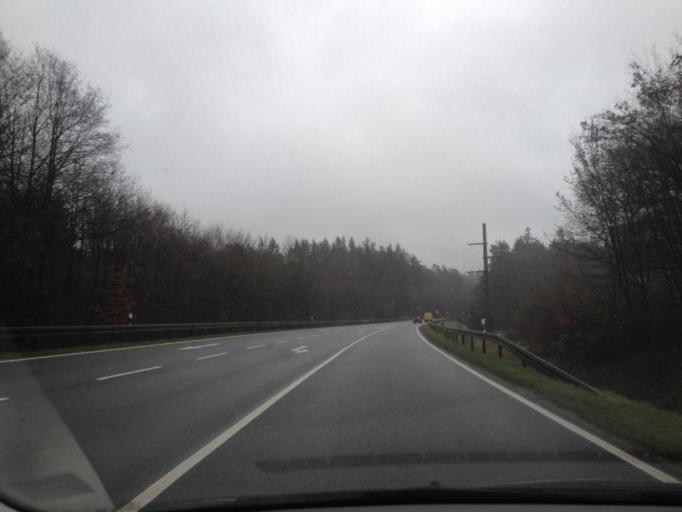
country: DE
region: Bavaria
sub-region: Regierungsbezirk Mittelfranken
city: Heroldsberg
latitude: 49.5254
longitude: 11.1675
